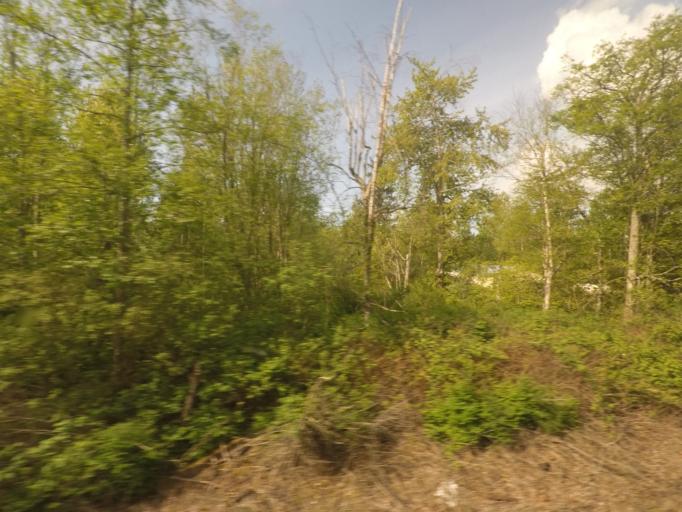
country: US
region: Washington
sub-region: Whatcom County
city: Marietta-Alderwood
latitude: 48.7866
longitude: -122.5555
